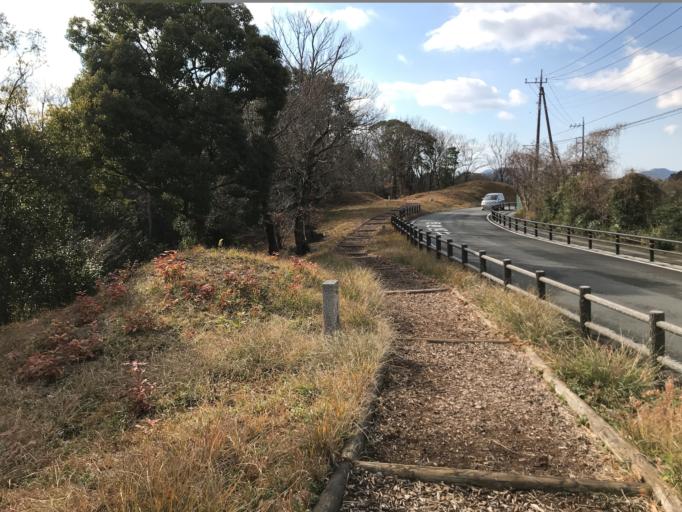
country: JP
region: Shizuoka
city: Mishima
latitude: 35.1071
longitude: 138.9435
